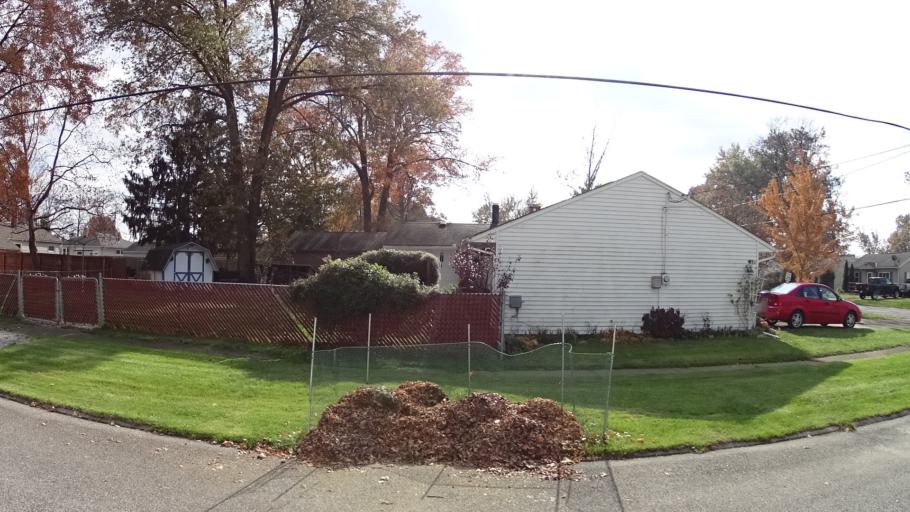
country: US
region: Ohio
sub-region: Lorain County
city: Elyria
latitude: 41.3845
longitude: -82.0821
